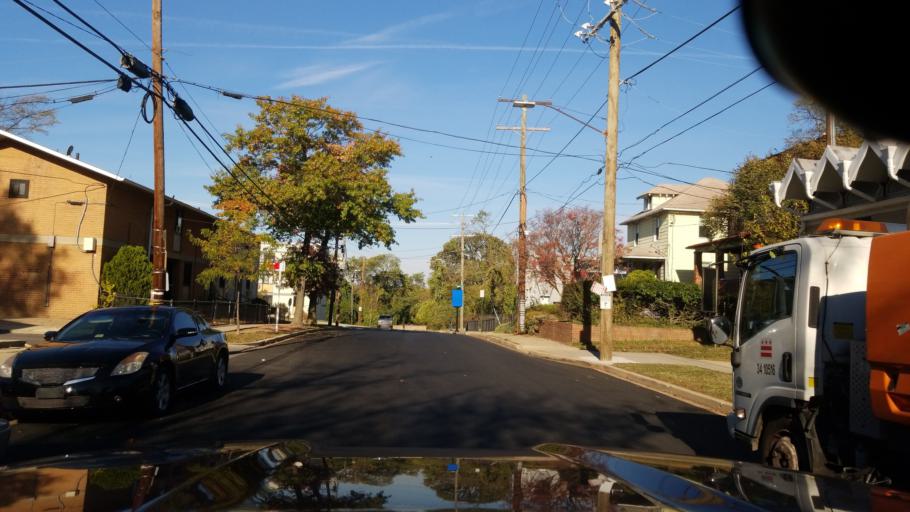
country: US
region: Maryland
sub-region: Prince George's County
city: Hillcrest Heights
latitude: 38.8576
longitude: -76.9729
